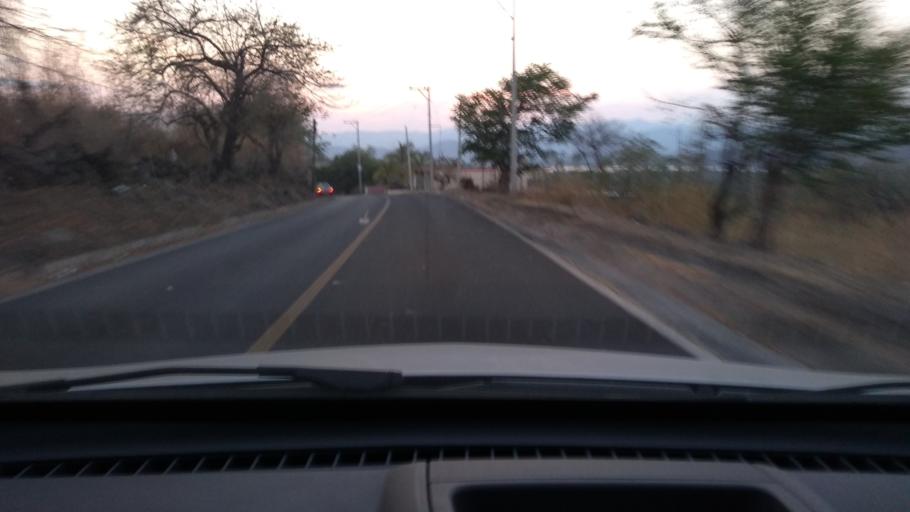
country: MX
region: Morelos
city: Coatetelco
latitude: 18.7221
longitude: -99.3111
